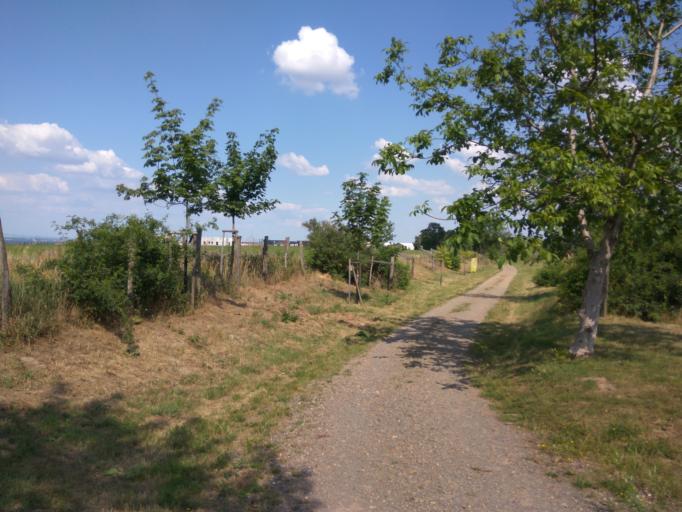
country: CZ
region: Central Bohemia
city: Nehvizdy
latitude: 50.1317
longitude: 14.7170
